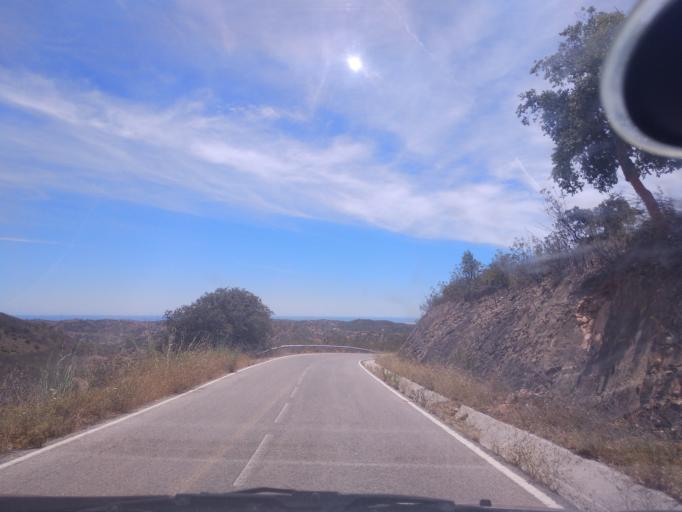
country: PT
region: Faro
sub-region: Sao Bras de Alportel
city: Sao Bras de Alportel
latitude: 37.1904
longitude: -7.7972
